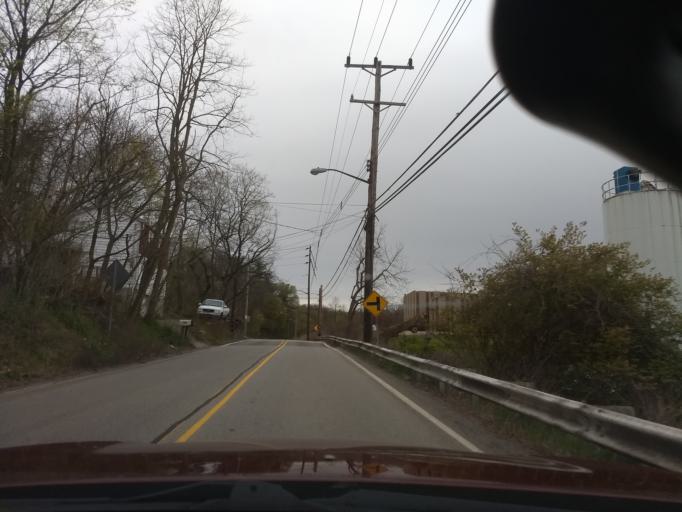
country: US
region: Pennsylvania
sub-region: Allegheny County
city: Mount Oliver
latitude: 40.3940
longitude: -79.9796
